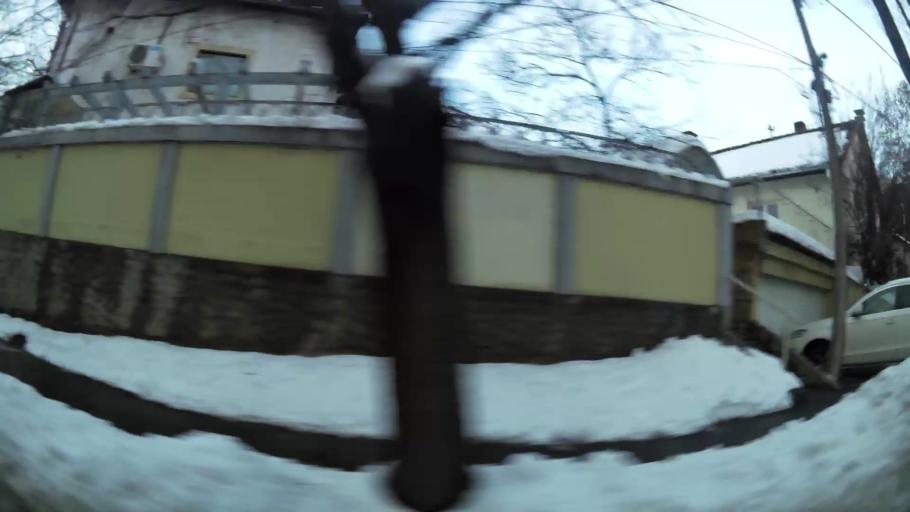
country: RS
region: Central Serbia
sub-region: Belgrade
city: Palilula
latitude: 44.7955
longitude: 20.5089
